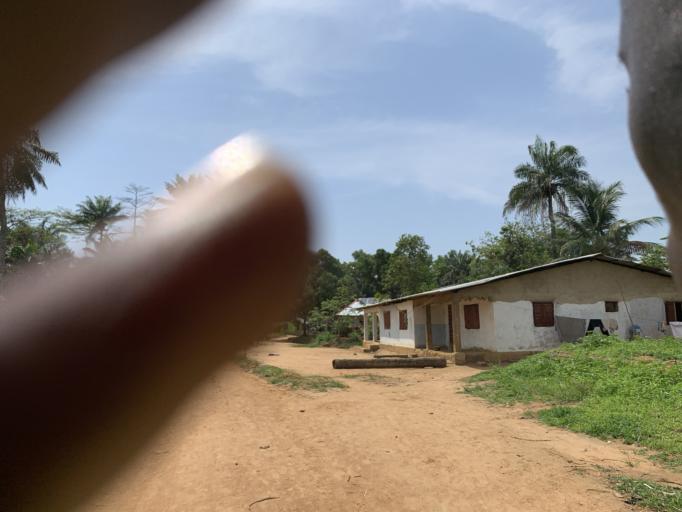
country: SL
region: Western Area
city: Waterloo
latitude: 8.3630
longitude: -13.0472
